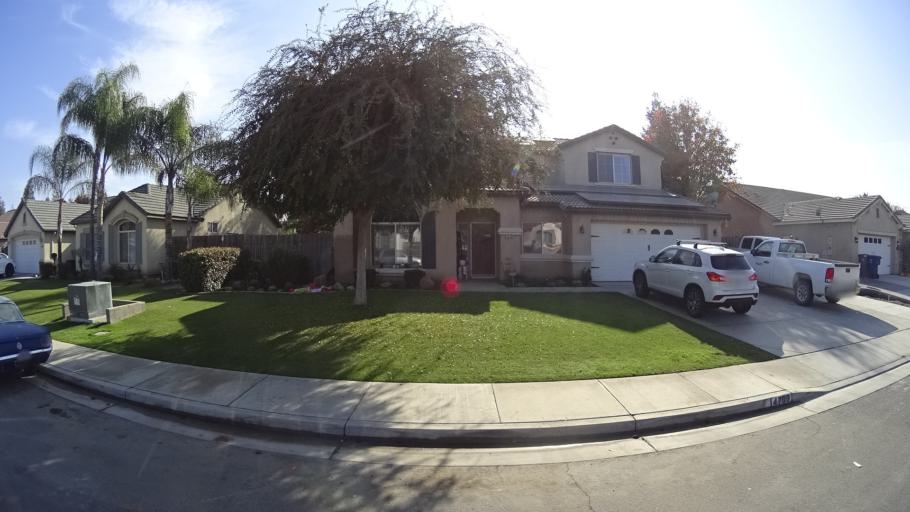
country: US
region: California
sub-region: Kern County
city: Rosedale
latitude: 35.3611
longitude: -119.1659
